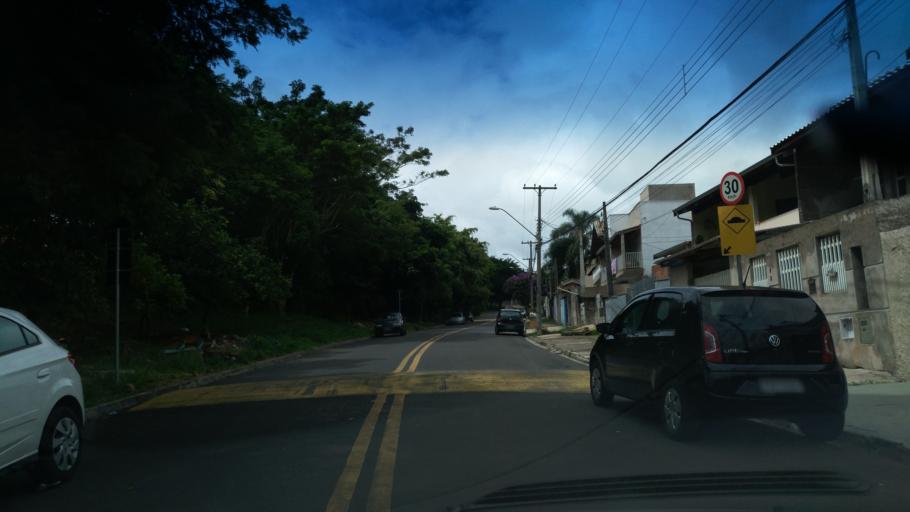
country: BR
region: Sao Paulo
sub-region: Valinhos
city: Valinhos
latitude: -22.9548
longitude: -46.9746
